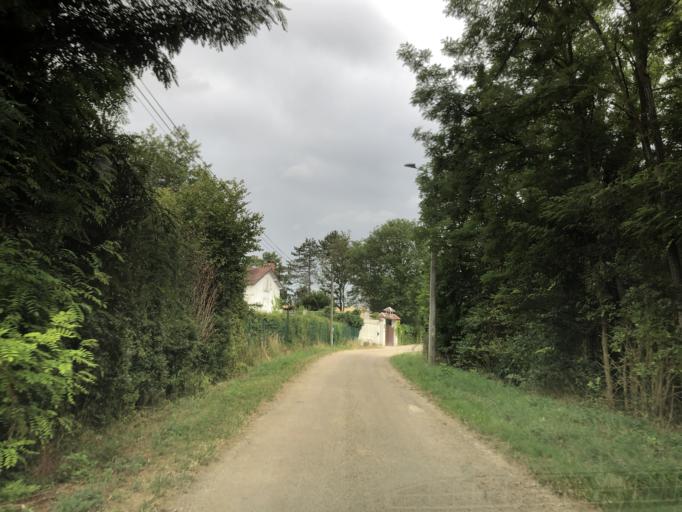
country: FR
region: Bourgogne
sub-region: Departement de l'Yonne
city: Laroche-Saint-Cydroine
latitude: 47.9476
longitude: 3.4477
